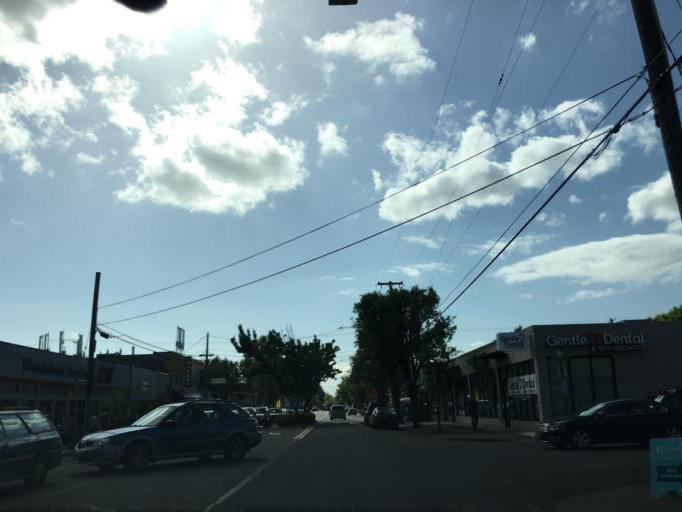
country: US
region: Oregon
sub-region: Clackamas County
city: Milwaukie
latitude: 45.4792
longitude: -122.6162
